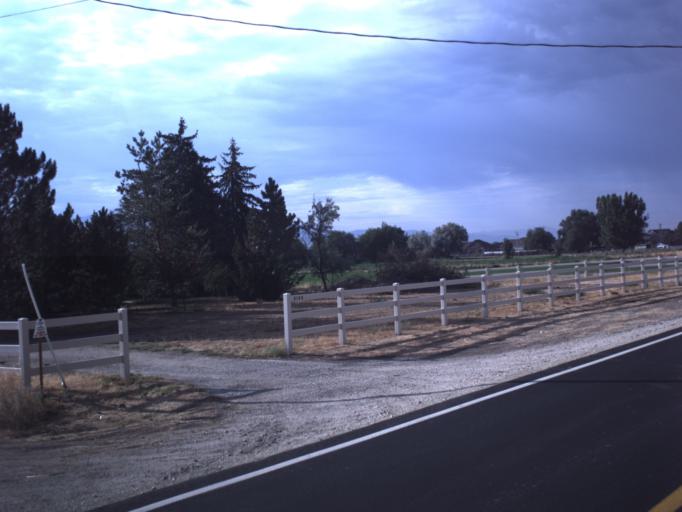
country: US
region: Utah
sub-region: Weber County
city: West Haven
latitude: 41.2092
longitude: -112.0930
